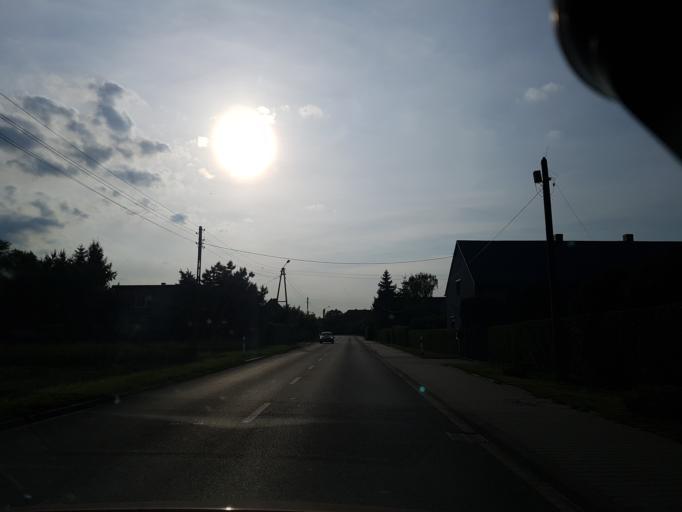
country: PL
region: Lower Silesian Voivodeship
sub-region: Powiat wroclawski
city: Gniechowice
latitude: 50.9834
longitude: 16.8467
